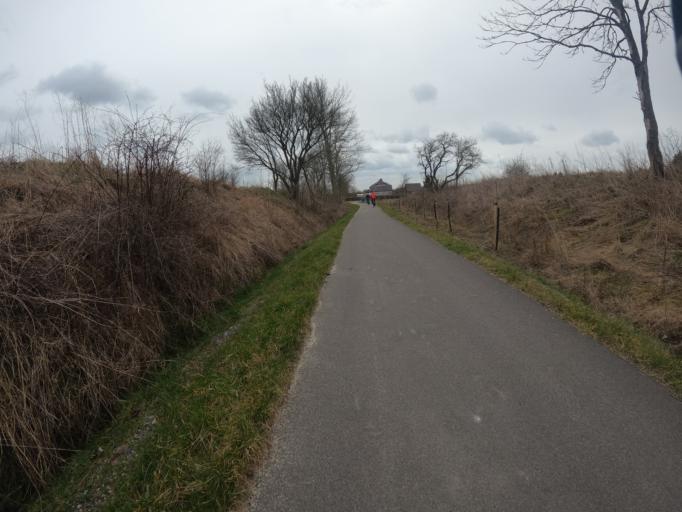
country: PL
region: West Pomeranian Voivodeship
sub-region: Powiat gryficki
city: Trzebiatow
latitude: 54.0776
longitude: 15.2602
